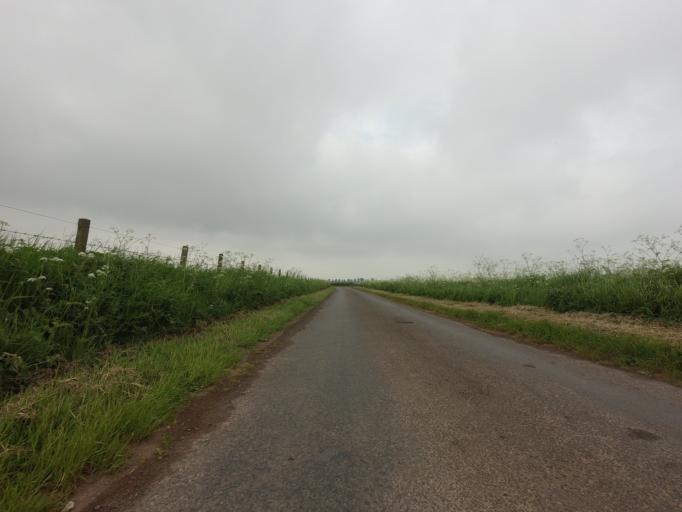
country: GB
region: Scotland
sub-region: Perth and Kinross
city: Milnathort
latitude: 56.2410
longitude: -3.3441
